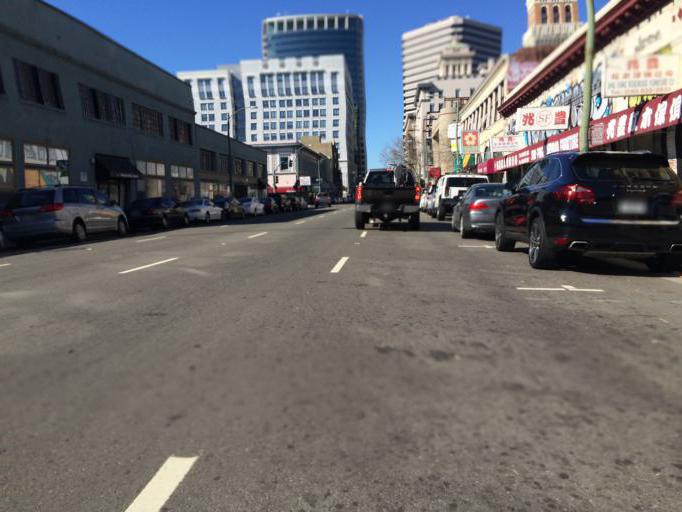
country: US
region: California
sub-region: Alameda County
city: Oakland
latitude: 37.8017
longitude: -122.2687
